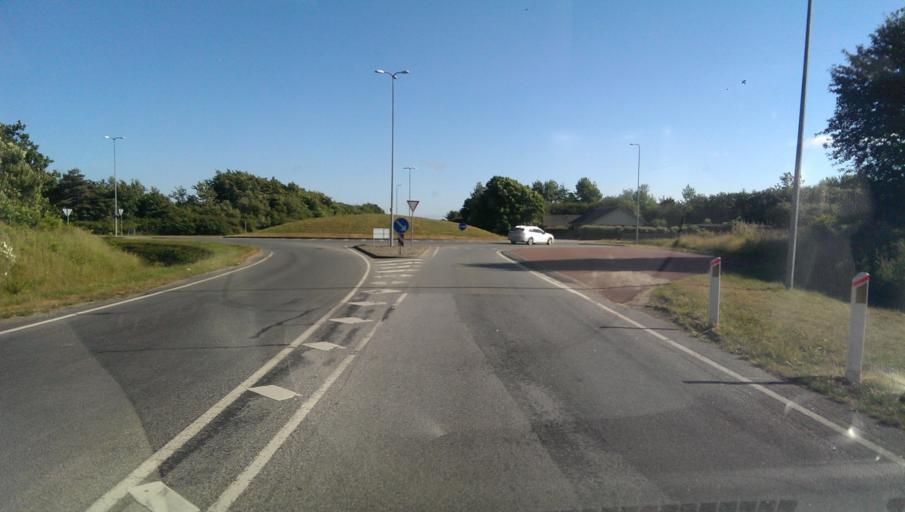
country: DK
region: South Denmark
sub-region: Esbjerg Kommune
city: Esbjerg
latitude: 55.5183
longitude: 8.4065
